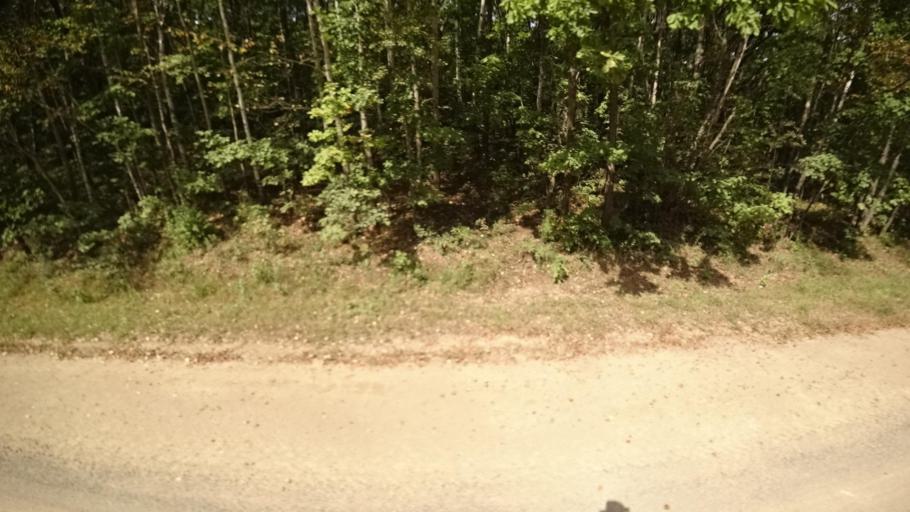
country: RU
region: Primorskiy
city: Yakovlevka
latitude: 44.6624
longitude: 133.6014
